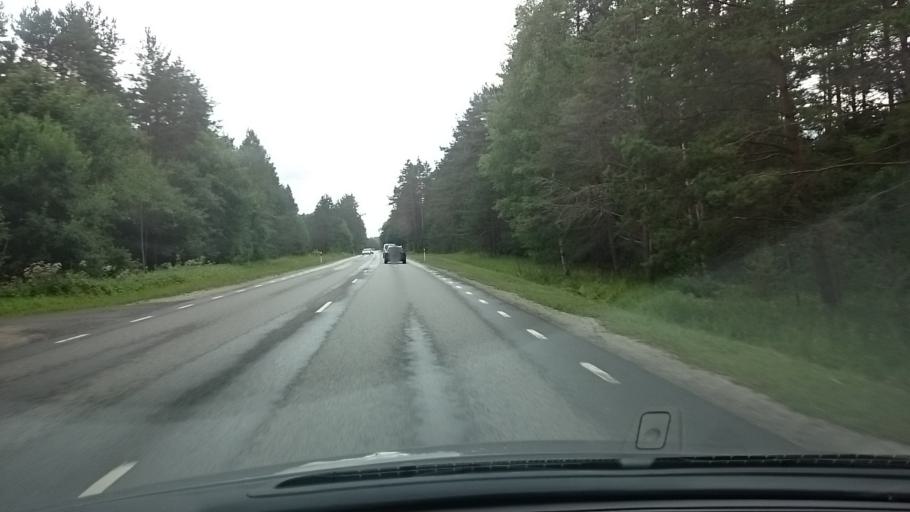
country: EE
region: Harju
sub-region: Nissi vald
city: Riisipere
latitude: 59.2490
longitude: 24.2803
